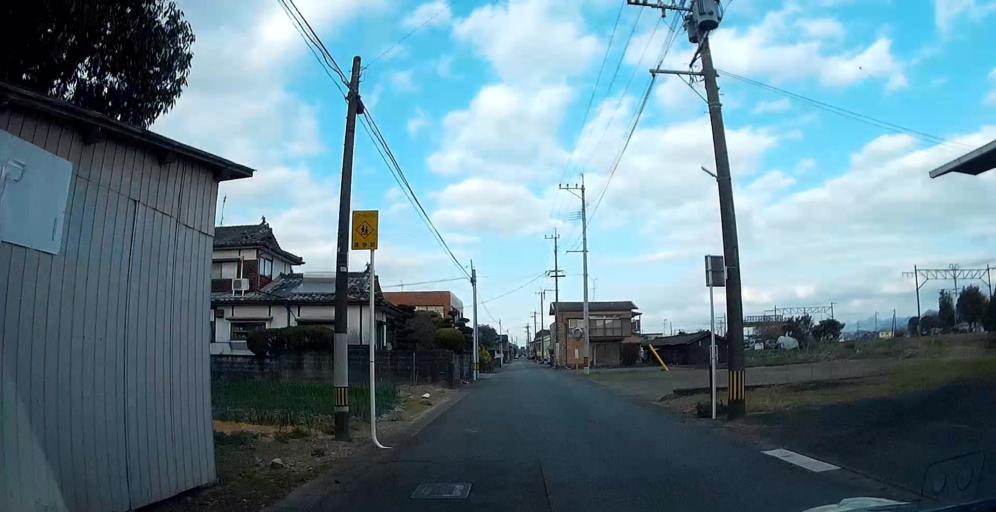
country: JP
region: Kumamoto
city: Yatsushiro
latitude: 32.5320
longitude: 130.6448
